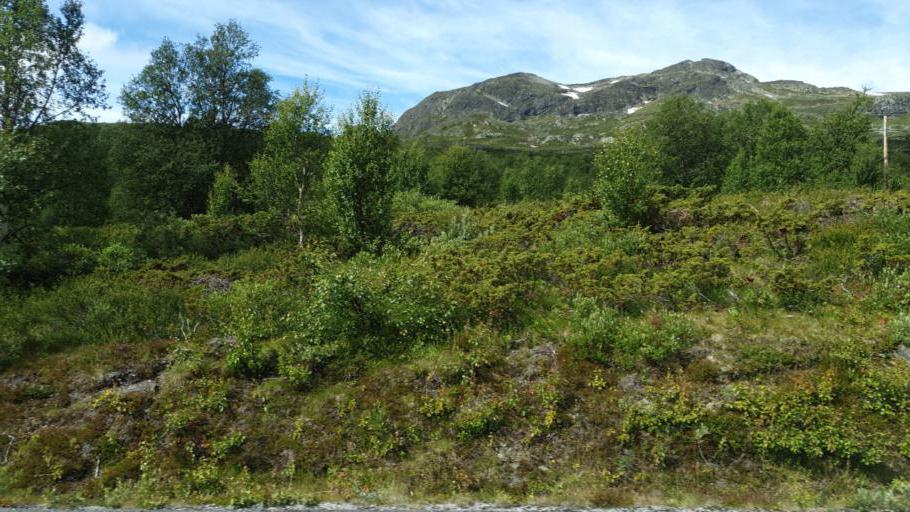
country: NO
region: Oppland
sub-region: Lom
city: Fossbergom
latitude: 61.5072
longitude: 8.8412
